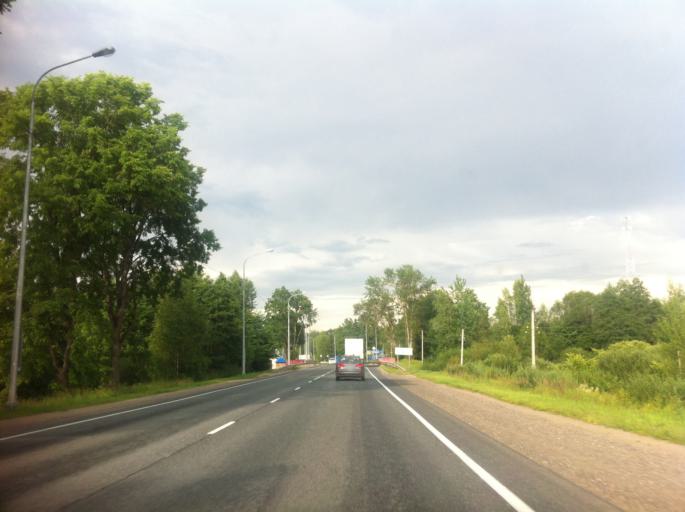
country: RU
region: Pskov
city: Plyussa
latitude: 58.2653
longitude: 29.4569
